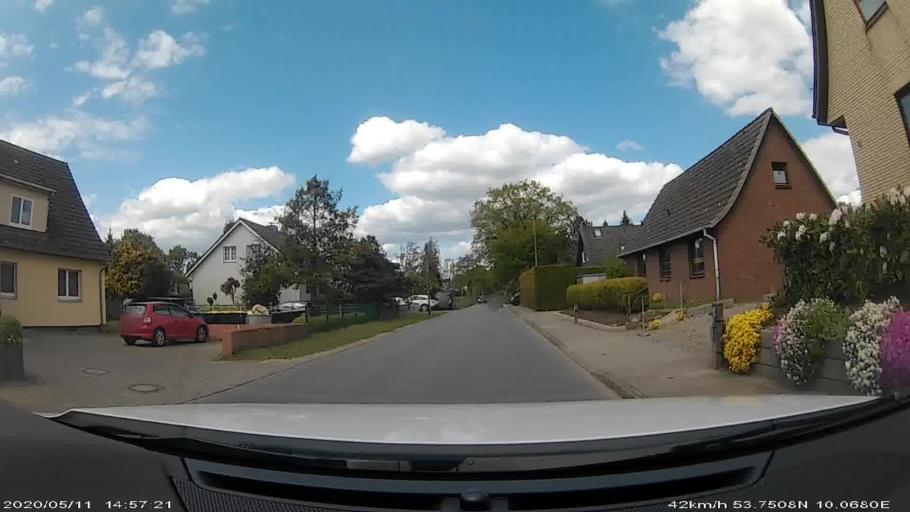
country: DE
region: Schleswig-Holstein
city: Tangstedt
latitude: 53.7651
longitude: 10.0721
